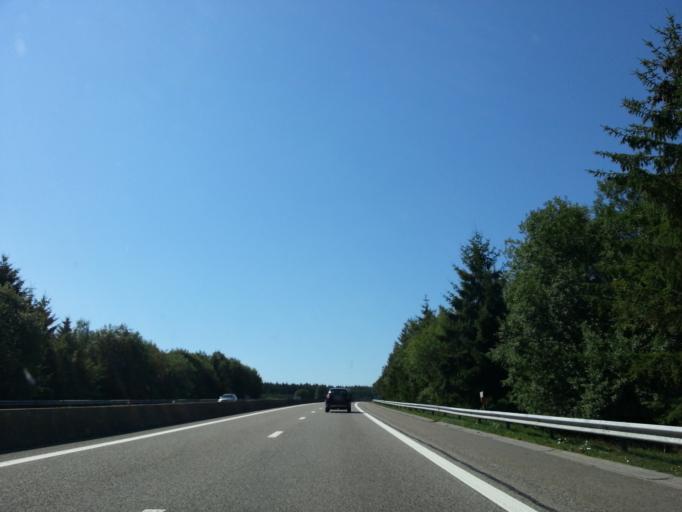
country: BE
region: Wallonia
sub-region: Province de Liege
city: Saint-Vith
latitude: 50.3286
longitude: 6.0904
